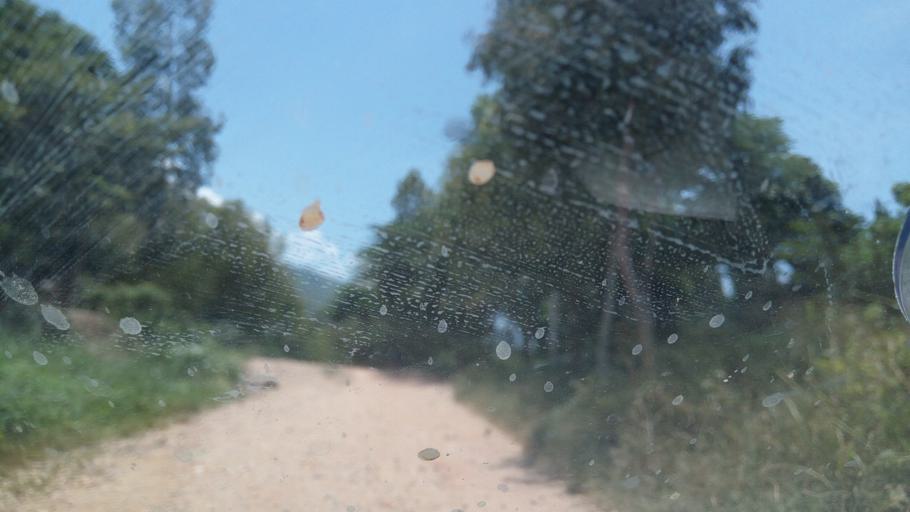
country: CD
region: South Kivu
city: Uvira
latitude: -3.4558
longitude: 29.1317
